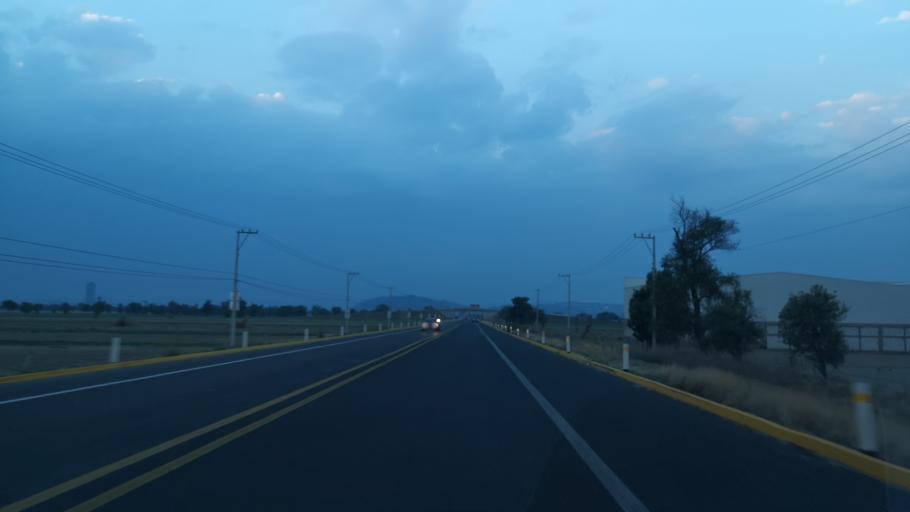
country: MX
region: Puebla
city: Santa Ana Xalmimilulco
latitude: 19.1892
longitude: -98.3684
